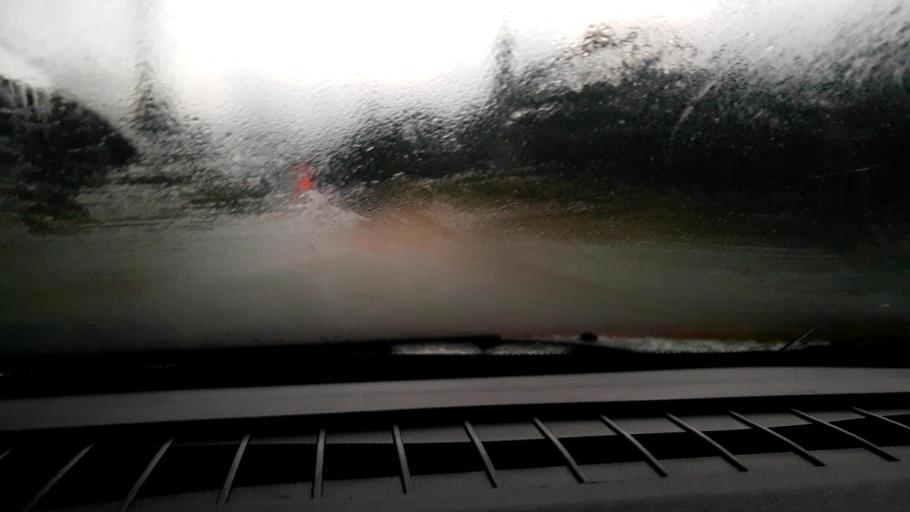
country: RU
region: Nizjnij Novgorod
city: Nizhniy Novgorod
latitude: 56.2368
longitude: 43.9897
